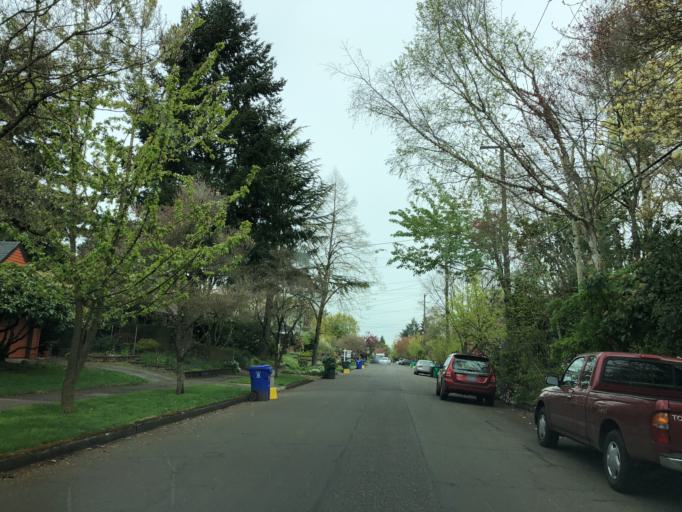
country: US
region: Oregon
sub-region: Multnomah County
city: Portland
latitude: 45.5544
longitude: -122.6338
